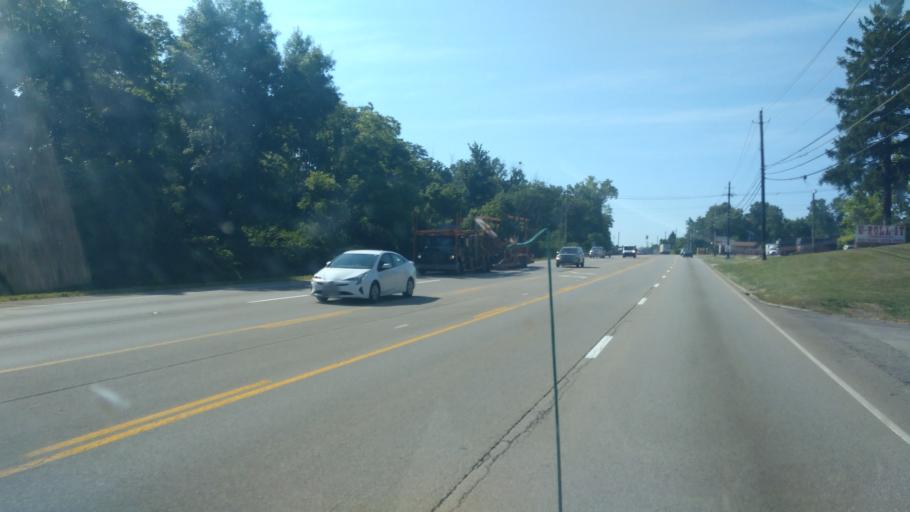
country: US
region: Ohio
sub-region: Delaware County
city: Delaware
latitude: 40.3208
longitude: -83.0702
